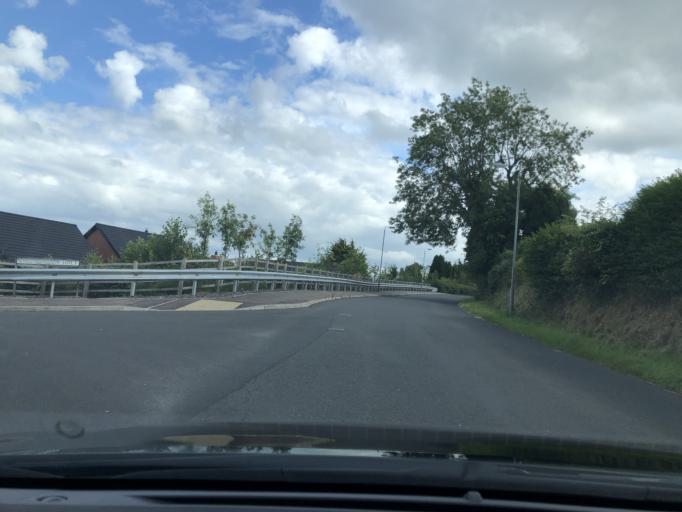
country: GB
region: Northern Ireland
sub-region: Ards District
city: Newtownards
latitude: 54.5874
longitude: -5.7136
